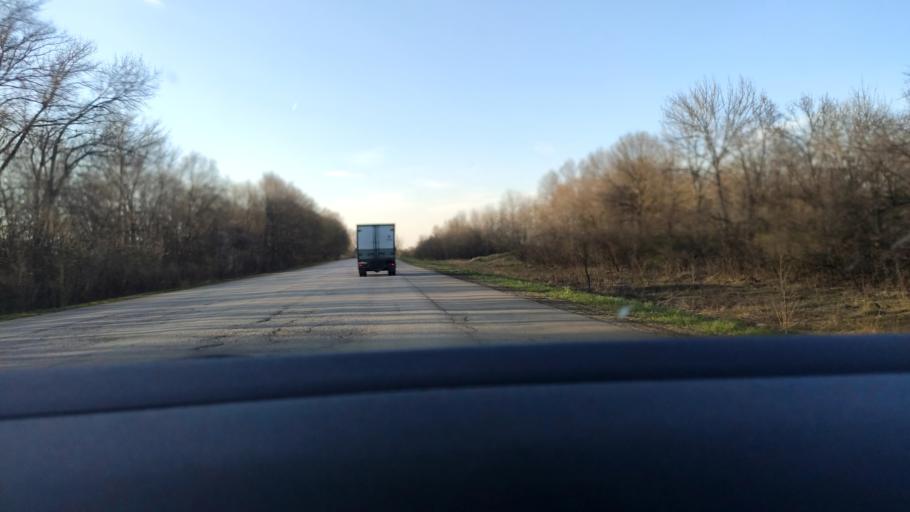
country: RU
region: Voronezj
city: Kolodeznyy
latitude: 51.2839
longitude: 39.0423
